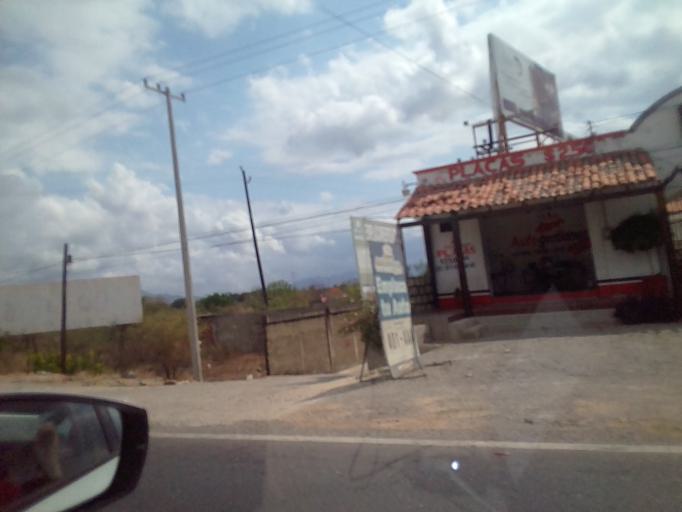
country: MX
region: Oaxaca
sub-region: Santo Domingo Tehuantepec
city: Santo Domingo Tehuantepec
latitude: 16.3094
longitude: -95.2358
